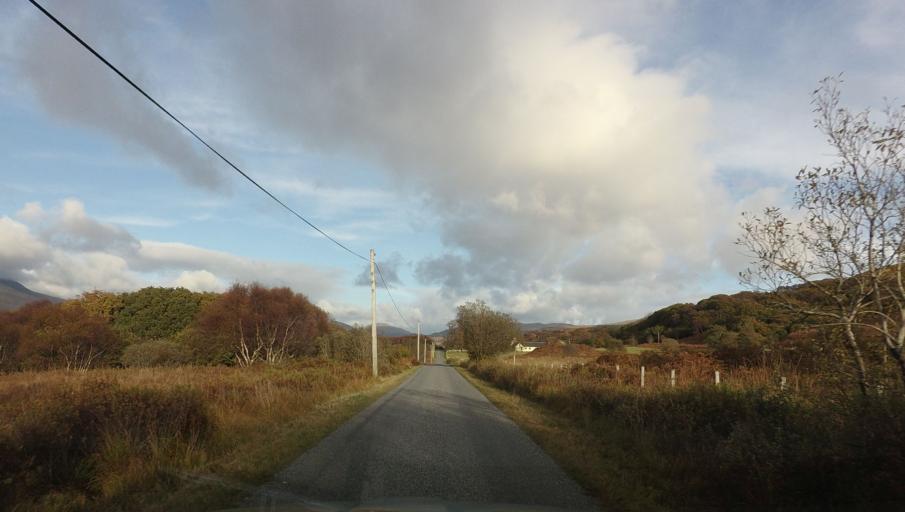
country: GB
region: Scotland
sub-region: Argyll and Bute
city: Isle Of Mull
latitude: 56.3556
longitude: -6.0668
